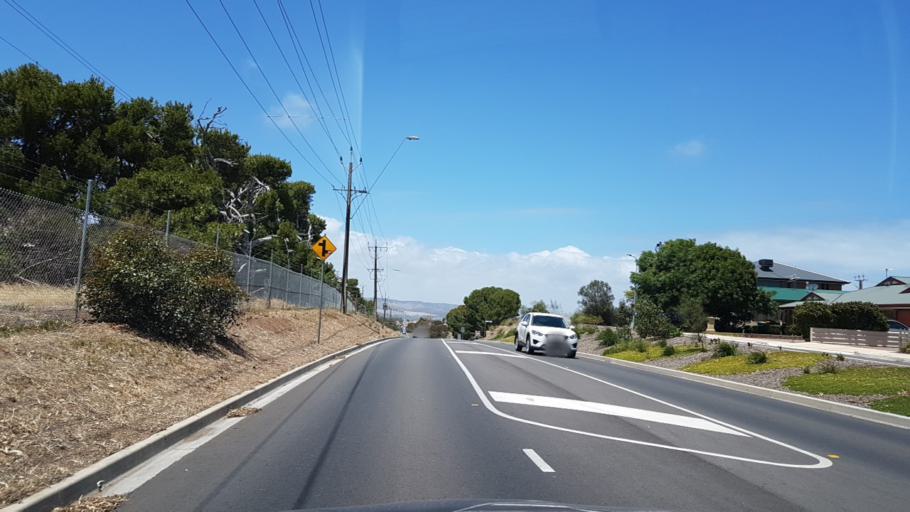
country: AU
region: South Australia
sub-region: Onkaparinga
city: Moana
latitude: -35.2315
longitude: 138.4807
